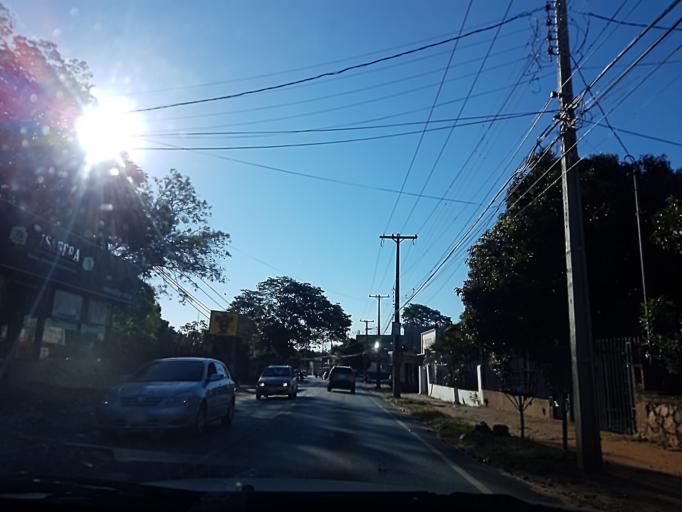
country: PY
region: Central
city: San Lorenzo
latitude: -25.2734
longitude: -57.4830
